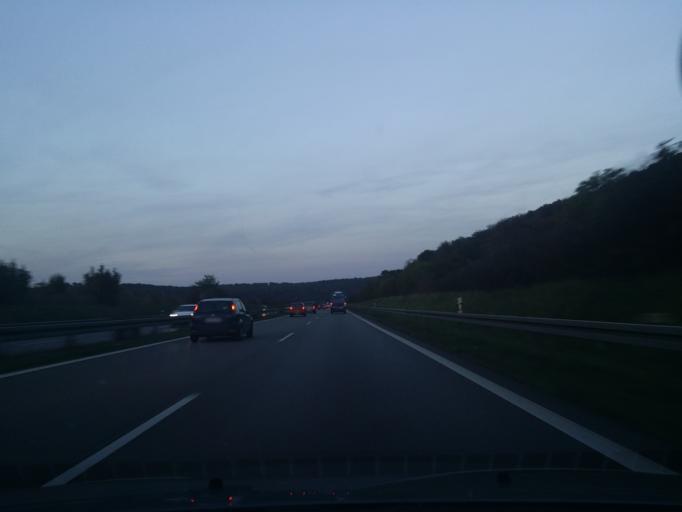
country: DE
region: Baden-Wuerttemberg
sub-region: Tuebingen Region
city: Kusterdingen
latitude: 48.5278
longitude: 9.1026
